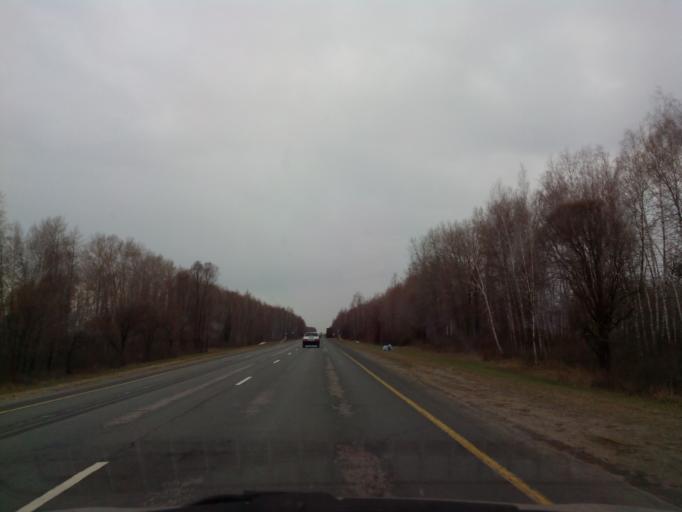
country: RU
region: Tambov
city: Michurinsk
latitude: 53.0616
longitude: 40.4485
